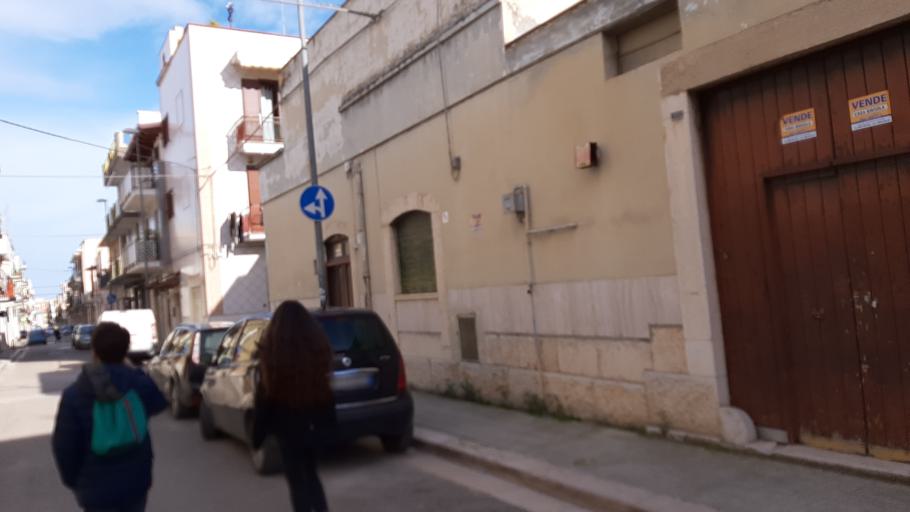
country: IT
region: Apulia
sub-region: Provincia di Barletta - Andria - Trani
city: Andria
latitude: 41.2315
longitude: 16.2933
